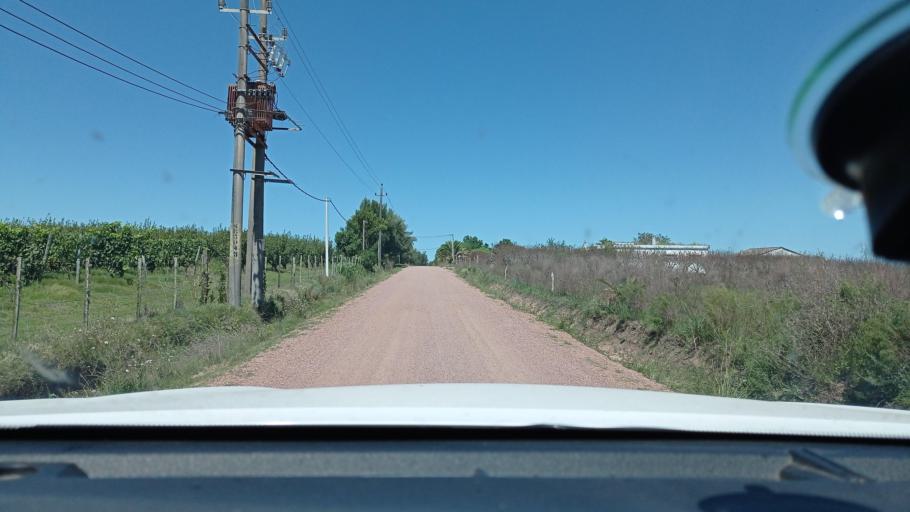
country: UY
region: Canelones
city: La Paz
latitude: -34.7487
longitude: -56.2001
